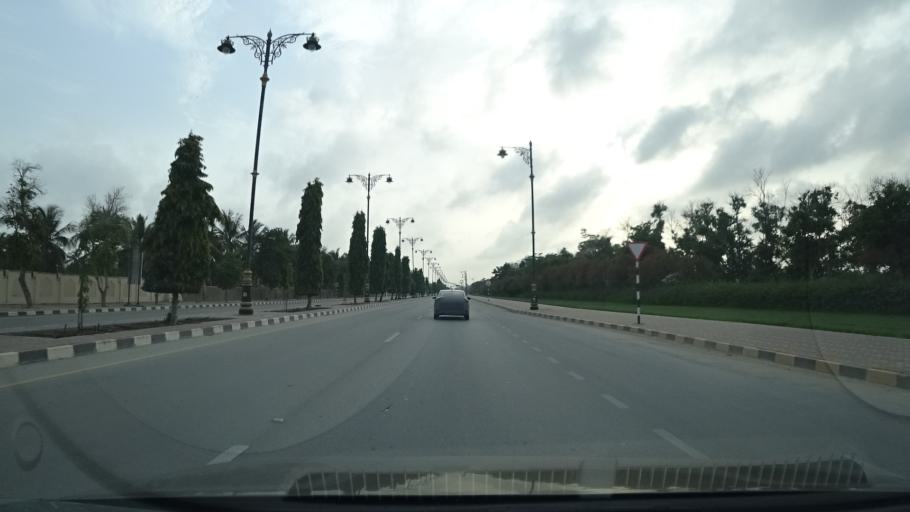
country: OM
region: Zufar
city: Salalah
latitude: 17.0260
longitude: 54.1662
